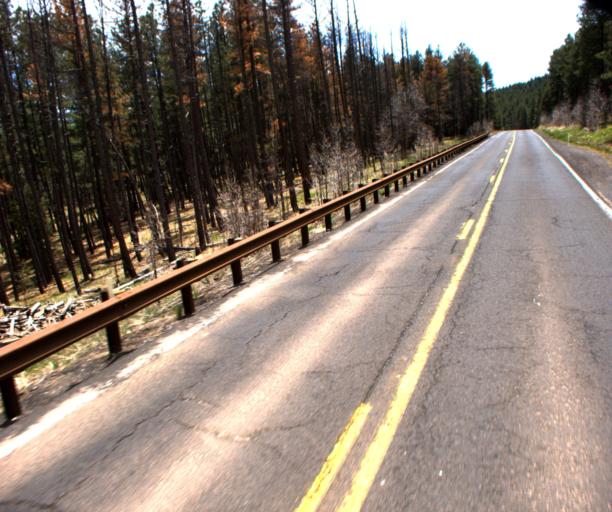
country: US
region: Arizona
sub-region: Coconino County
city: Kachina Village
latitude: 35.0689
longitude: -111.7321
